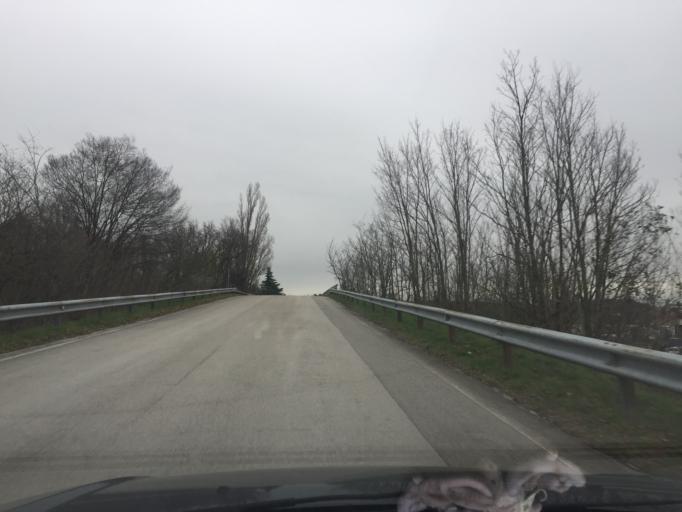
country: IT
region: Friuli Venezia Giulia
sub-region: Provincia di Trieste
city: Zolla
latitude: 45.7016
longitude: 13.8290
